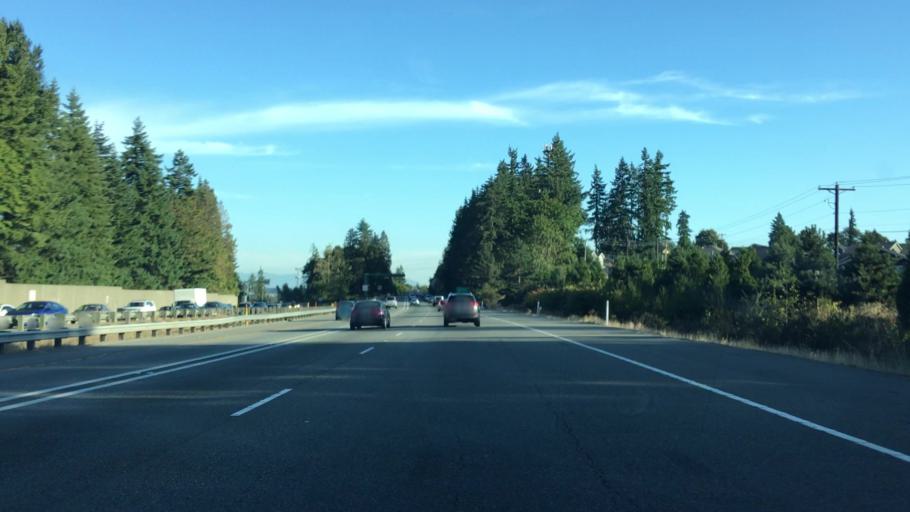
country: US
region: Washington
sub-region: Snohomish County
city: Martha Lake
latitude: 47.8179
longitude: -122.2396
